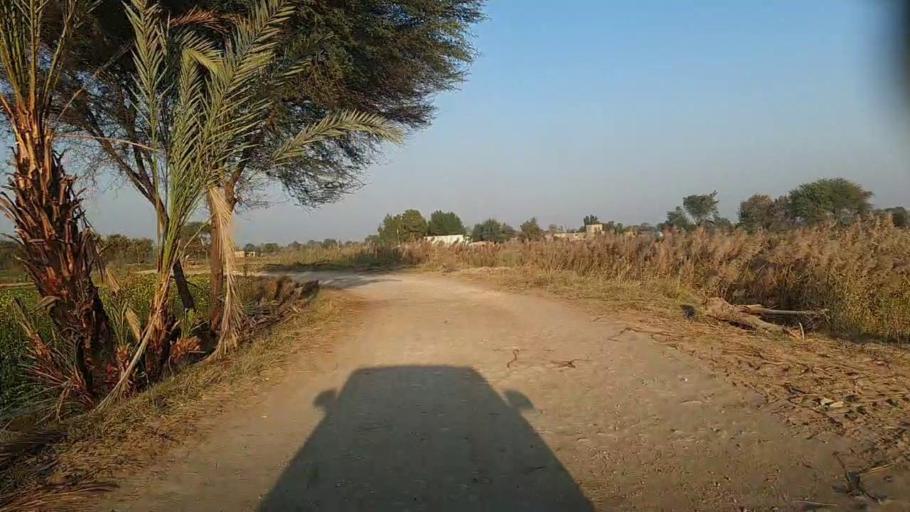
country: PK
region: Sindh
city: Mirpur Mathelo
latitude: 27.8794
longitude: 69.6499
